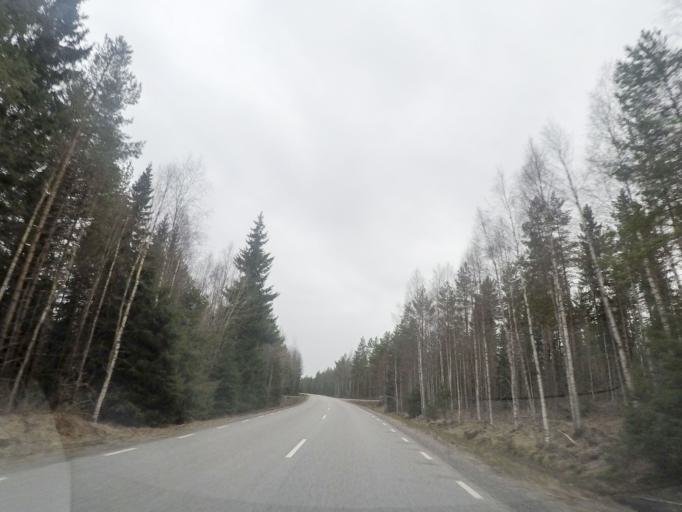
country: SE
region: Dalarna
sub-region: Ludvika Kommun
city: Abborrberget
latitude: 60.0577
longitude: 14.7989
